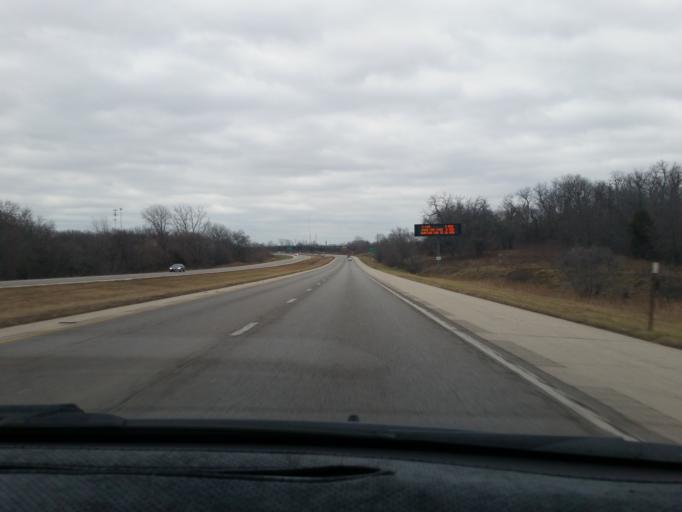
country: US
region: Kansas
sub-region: Johnson County
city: Olathe
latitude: 38.9440
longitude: -94.8739
